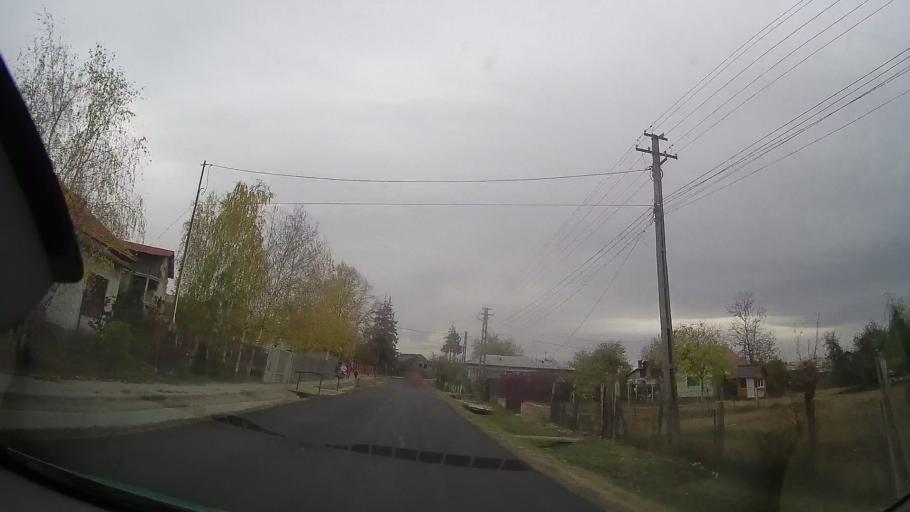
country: RO
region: Prahova
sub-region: Comuna Fantanele
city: Fantanele
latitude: 45.0072
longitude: 26.3769
